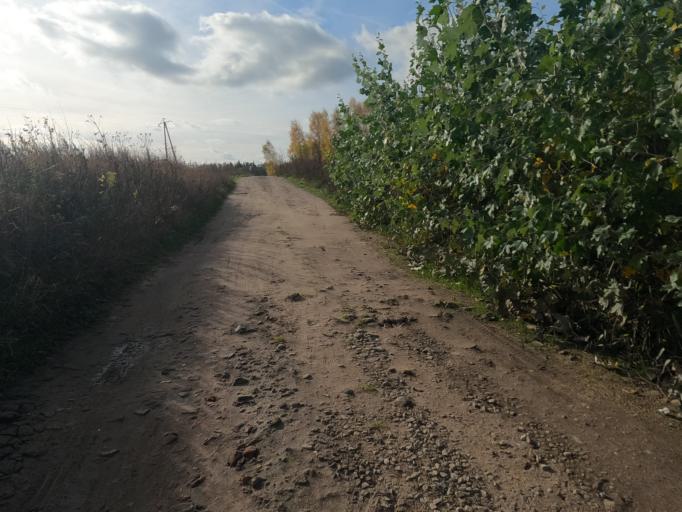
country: PL
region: Pomeranian Voivodeship
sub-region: Powiat starogardzki
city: Starogard Gdanski
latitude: 53.9741
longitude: 18.4828
